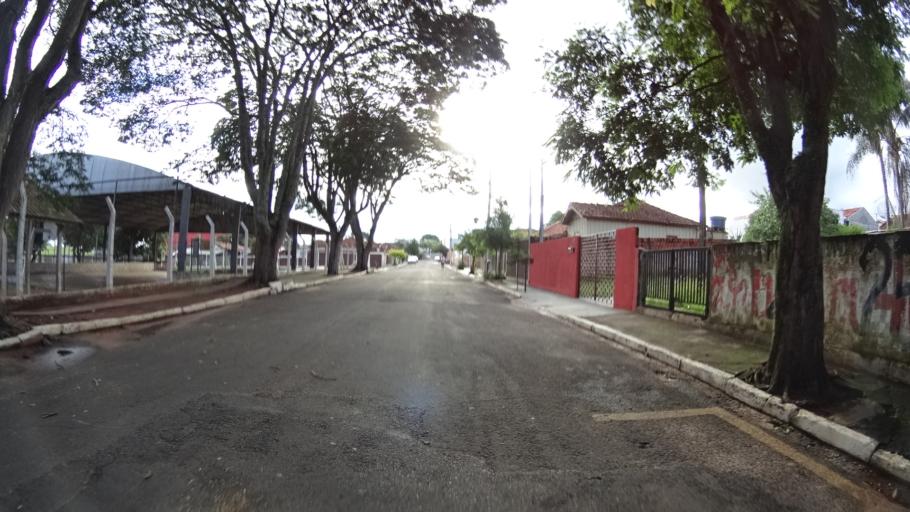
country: BR
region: Sao Paulo
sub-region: Marilia
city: Marilia
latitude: -22.2224
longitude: -49.8888
